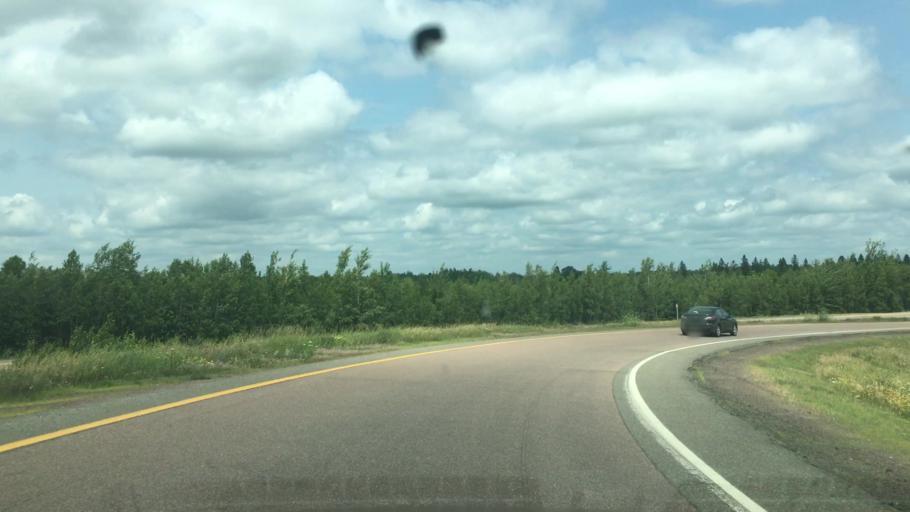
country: CA
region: New Brunswick
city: Dieppe
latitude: 46.1288
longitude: -64.6831
